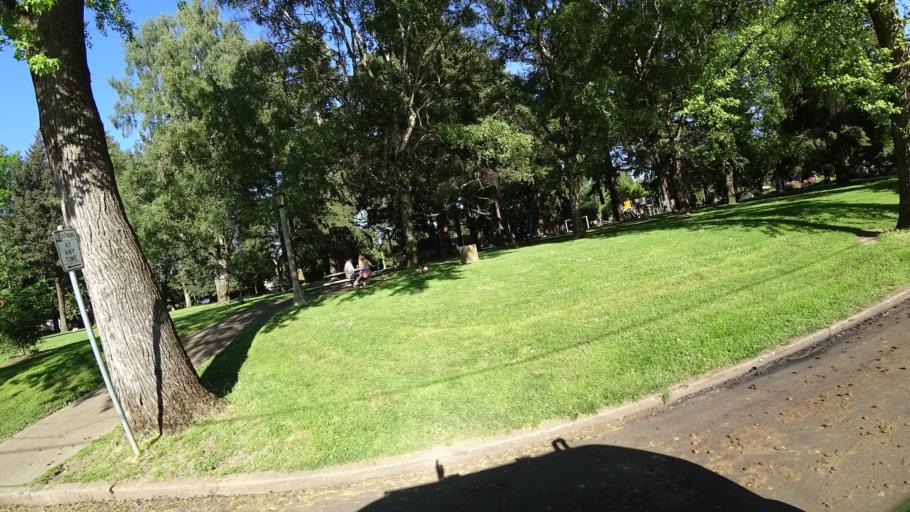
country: US
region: Oregon
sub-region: Multnomah County
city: Portland
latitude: 45.5277
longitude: -122.6359
